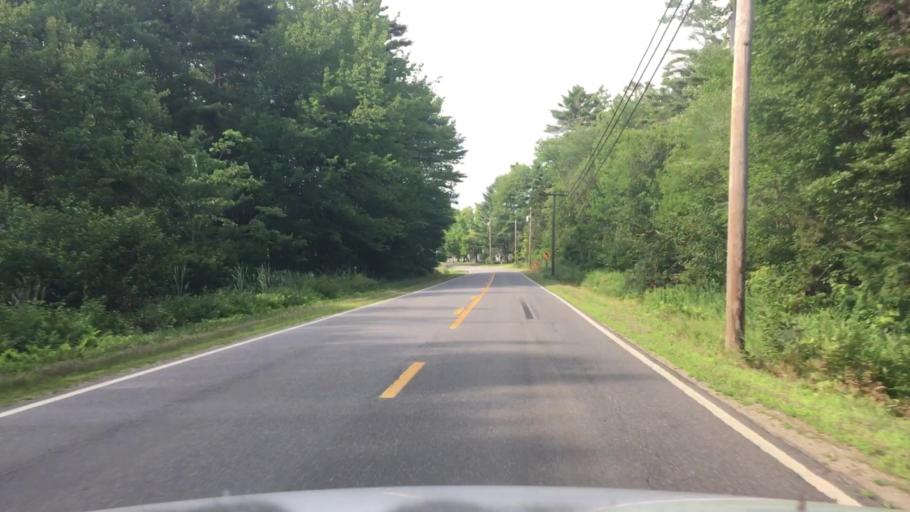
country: US
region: Maine
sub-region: Lincoln County
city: Waldoboro
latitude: 44.1156
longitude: -69.3650
